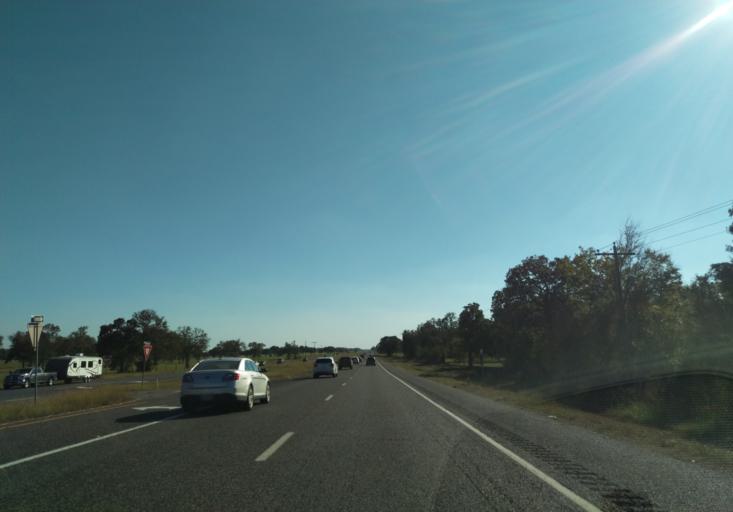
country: US
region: Texas
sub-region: Waller County
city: Hempstead
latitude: 30.1613
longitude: -96.0677
